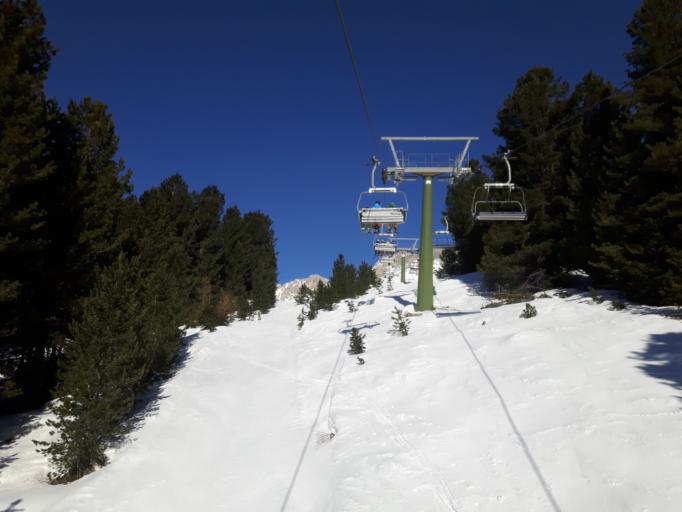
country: IT
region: Trentino-Alto Adige
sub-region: Provincia di Trento
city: Panchia
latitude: 46.3456
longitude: 11.5434
